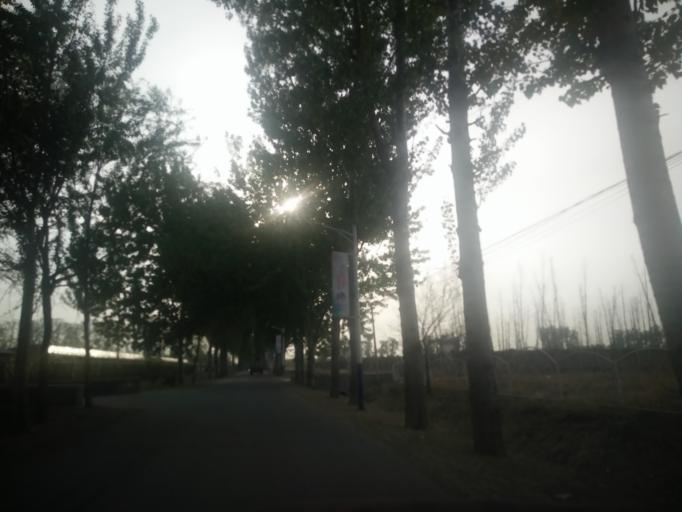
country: CN
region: Beijing
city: Weishanzhuang
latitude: 39.6752
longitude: 116.4370
